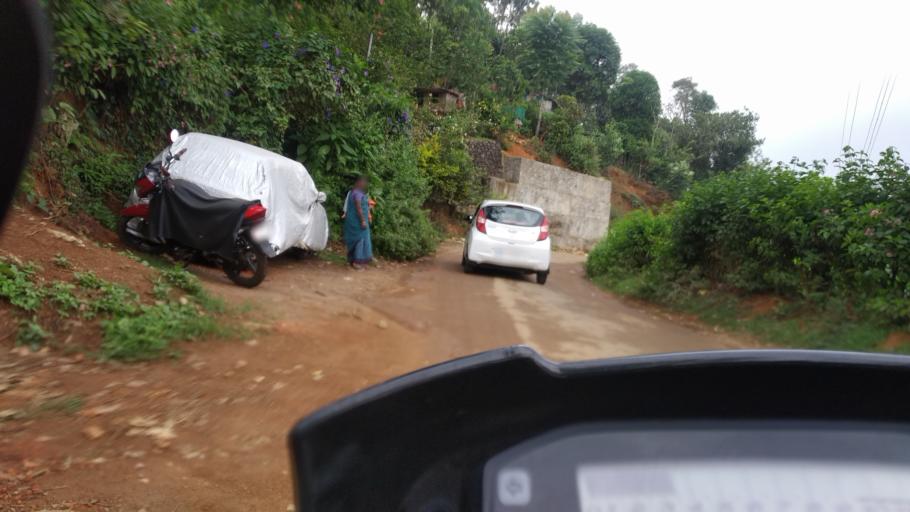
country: IN
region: Kerala
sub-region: Kottayam
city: Erattupetta
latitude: 9.5845
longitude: 77.0099
